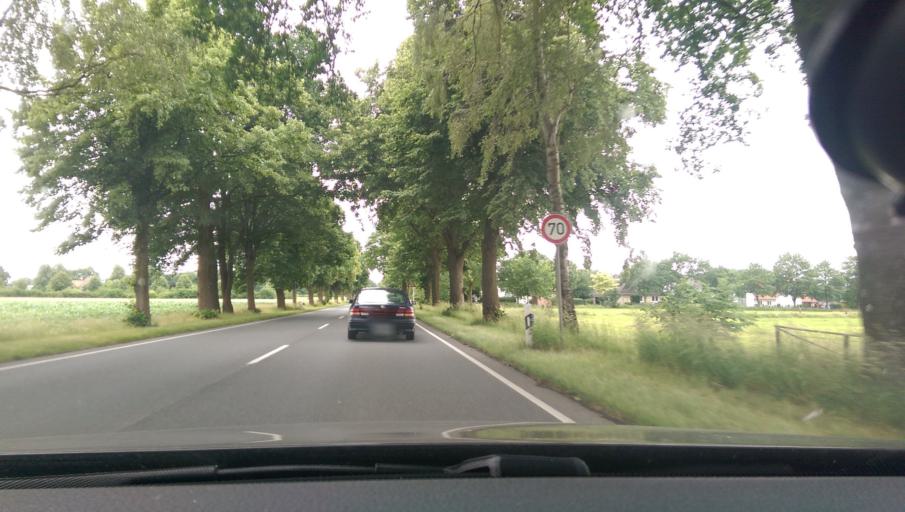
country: DE
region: Lower Saxony
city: Kirchlinteln
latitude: 52.9820
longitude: 9.2612
